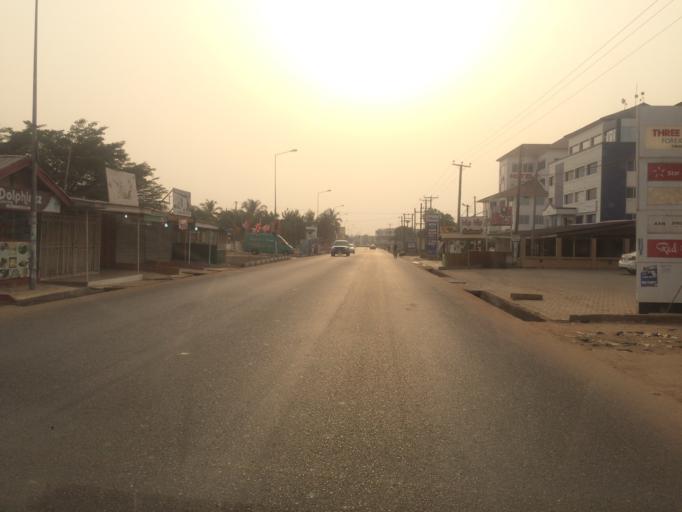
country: GH
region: Greater Accra
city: Nungua
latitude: 5.6273
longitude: -0.0863
